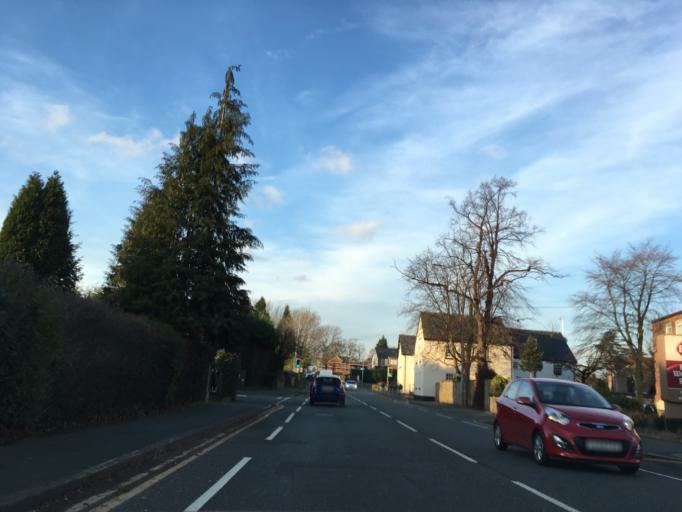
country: GB
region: England
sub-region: Cheshire East
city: Wilmslow
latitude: 53.3535
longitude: -2.2166
